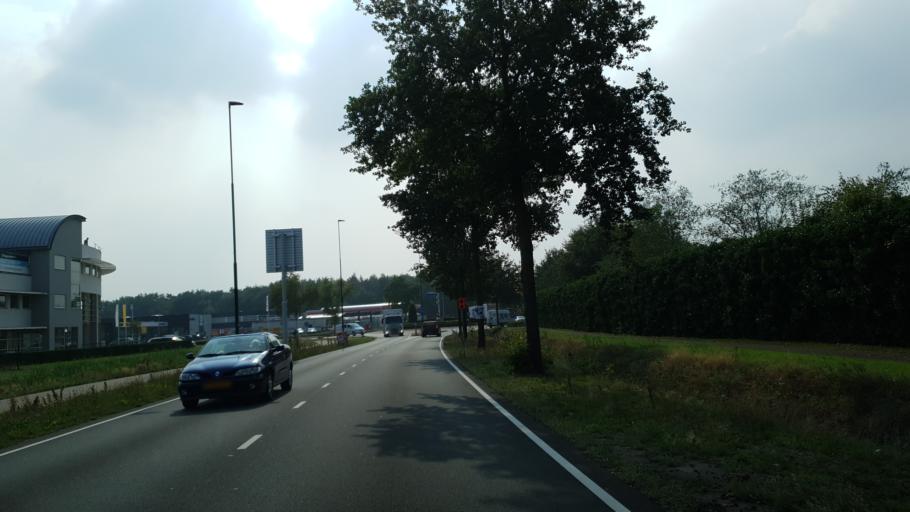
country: NL
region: North Brabant
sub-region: Gemeente Valkenswaard
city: Valkenswaard
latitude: 51.3417
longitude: 5.4648
